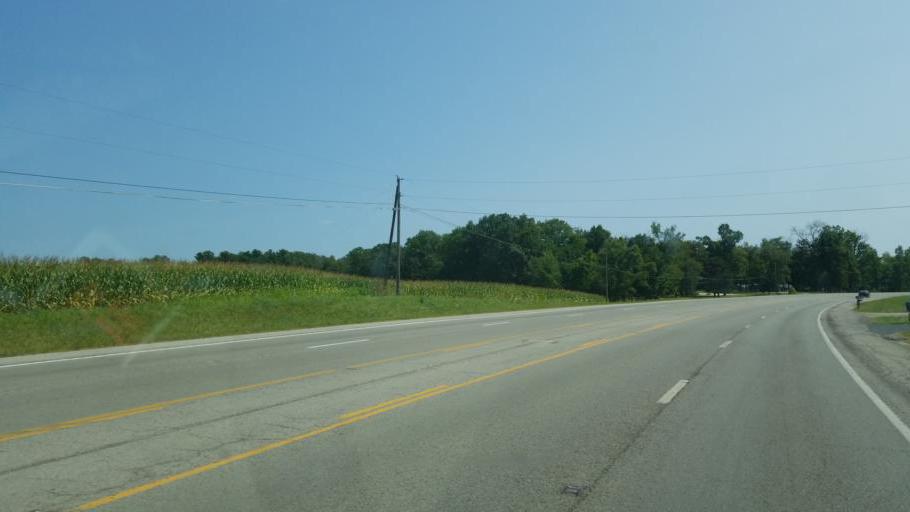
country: US
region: Ohio
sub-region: Richland County
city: Shelby
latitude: 40.8367
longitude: -82.6060
